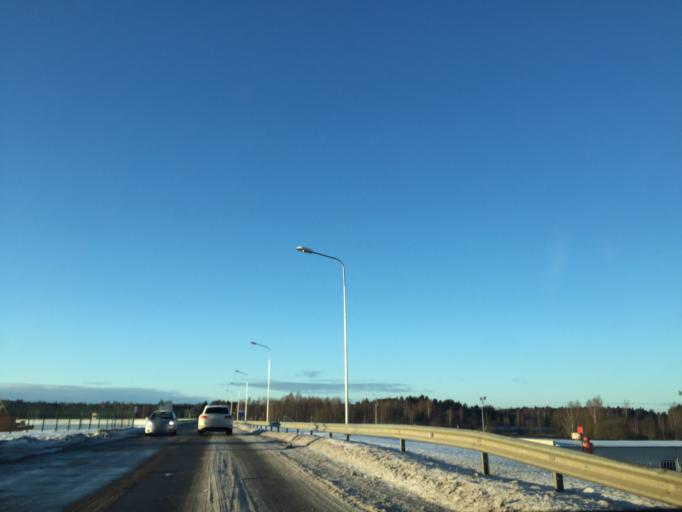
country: LV
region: Kegums
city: Kegums
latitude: 56.7388
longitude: 24.7070
